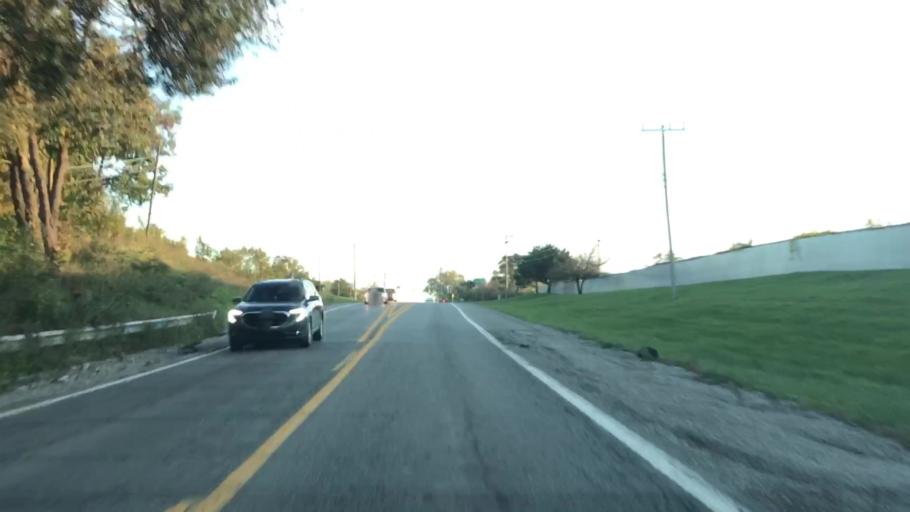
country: US
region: Michigan
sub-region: Macomb County
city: Shelby
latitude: 42.6547
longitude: -83.0732
